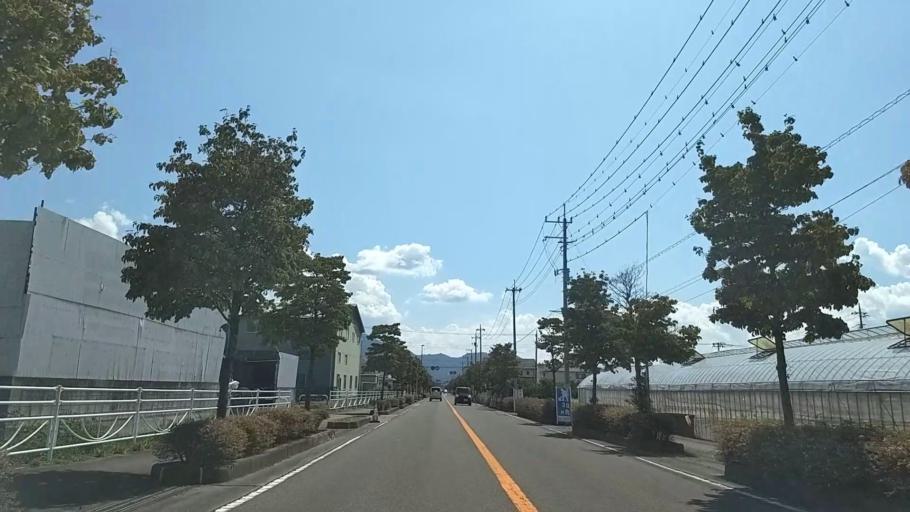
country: JP
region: Yamanashi
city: Ryuo
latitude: 35.6011
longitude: 138.5044
